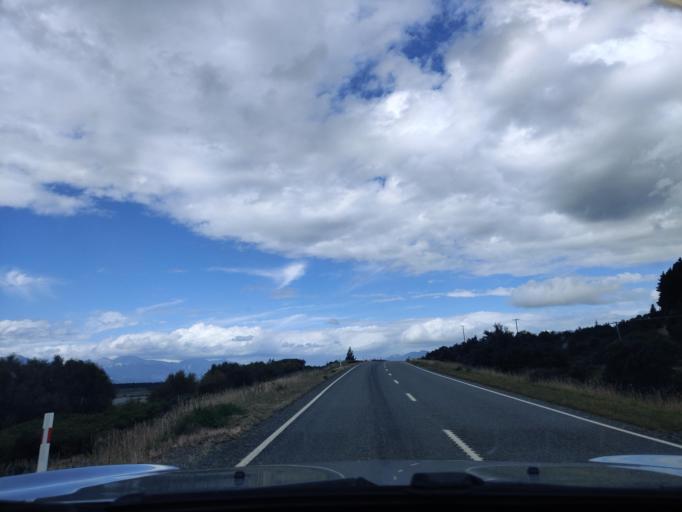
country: NZ
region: Canterbury
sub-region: Hurunui District
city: Amberley
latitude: -42.5695
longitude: 172.6943
